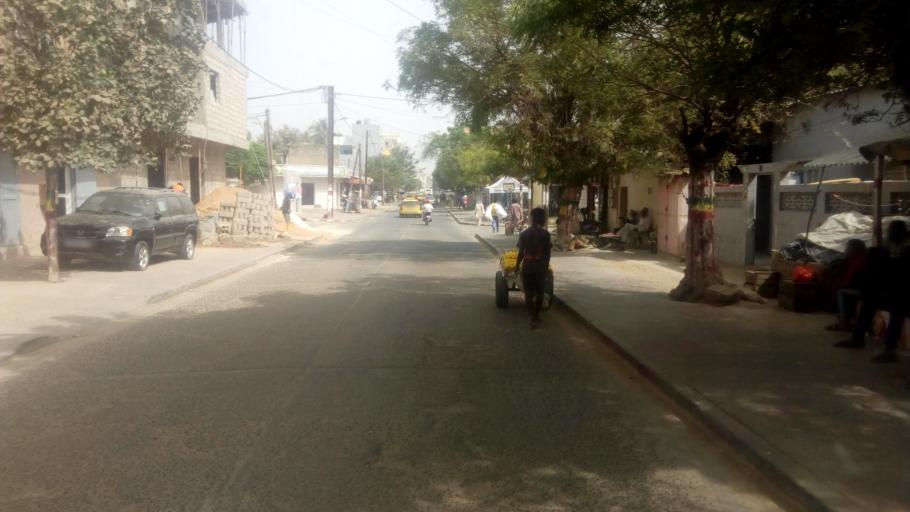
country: SN
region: Dakar
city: Grand Dakar
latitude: 14.7250
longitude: -17.4528
